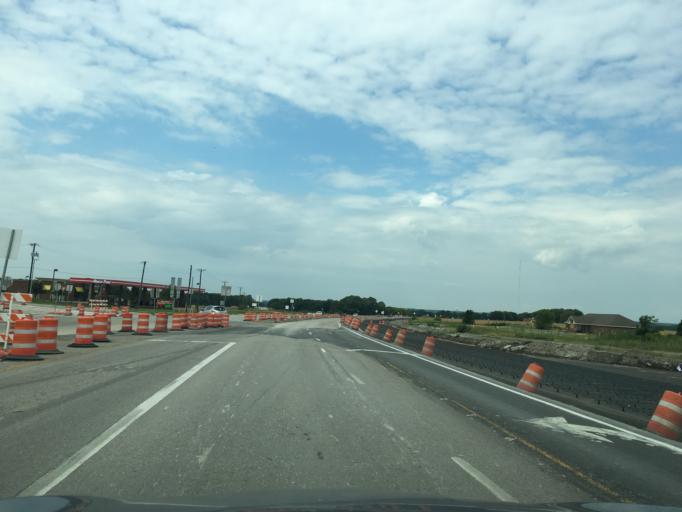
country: US
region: Texas
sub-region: Collin County
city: Melissa
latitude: 33.2678
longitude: -96.5861
